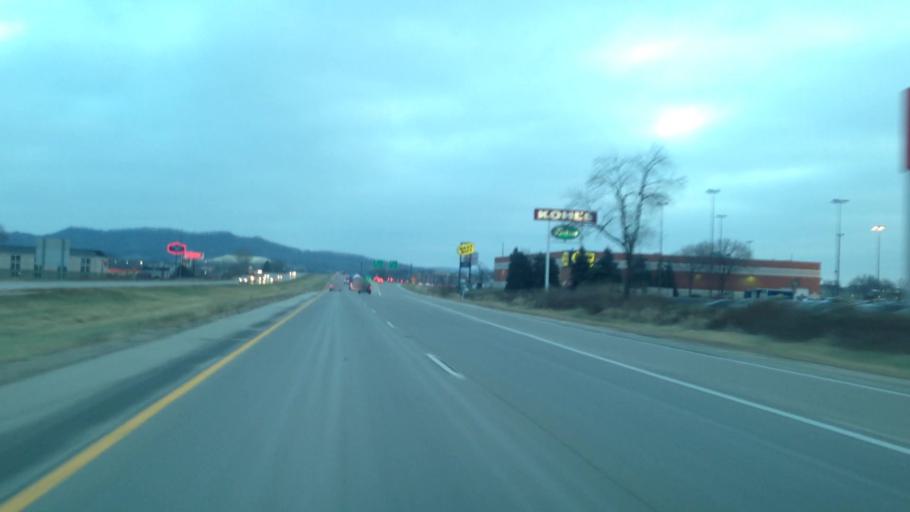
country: US
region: Wisconsin
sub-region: La Crosse County
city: Onalaska
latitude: 43.8769
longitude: -91.1942
